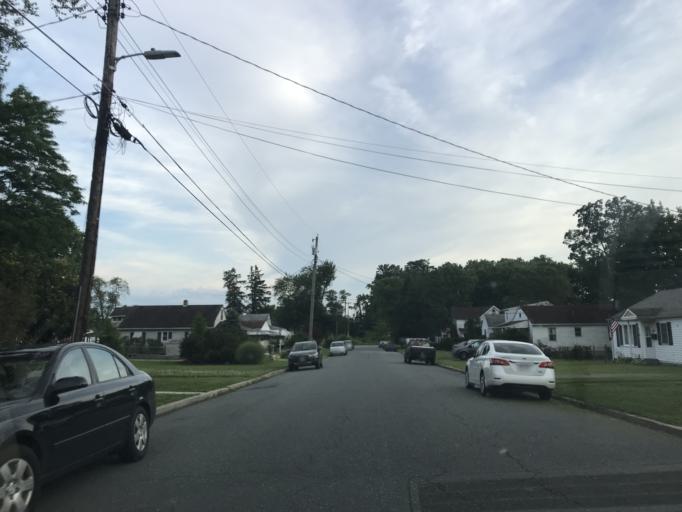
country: US
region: Maryland
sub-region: Harford County
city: Aberdeen
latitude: 39.5034
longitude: -76.1696
